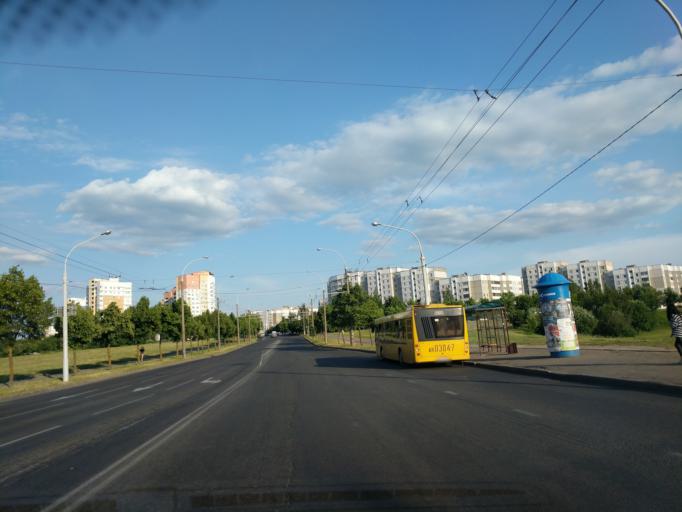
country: BY
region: Minsk
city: Malinovka
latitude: 53.8541
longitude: 27.4470
